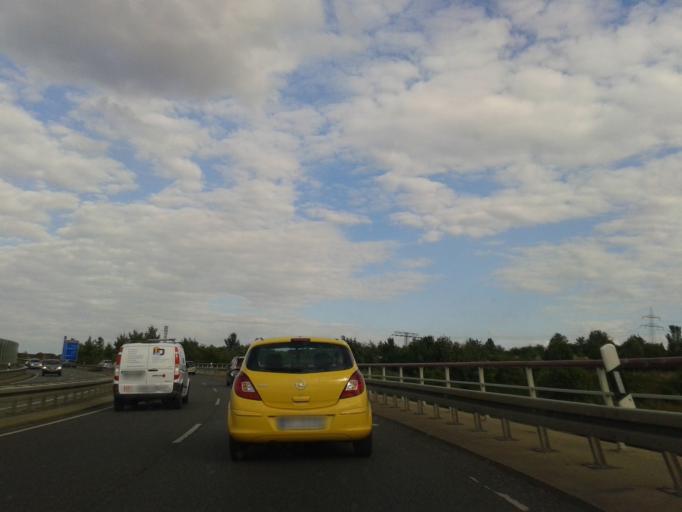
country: DE
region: Saxony
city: Bannewitz
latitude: 51.0111
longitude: 13.7250
